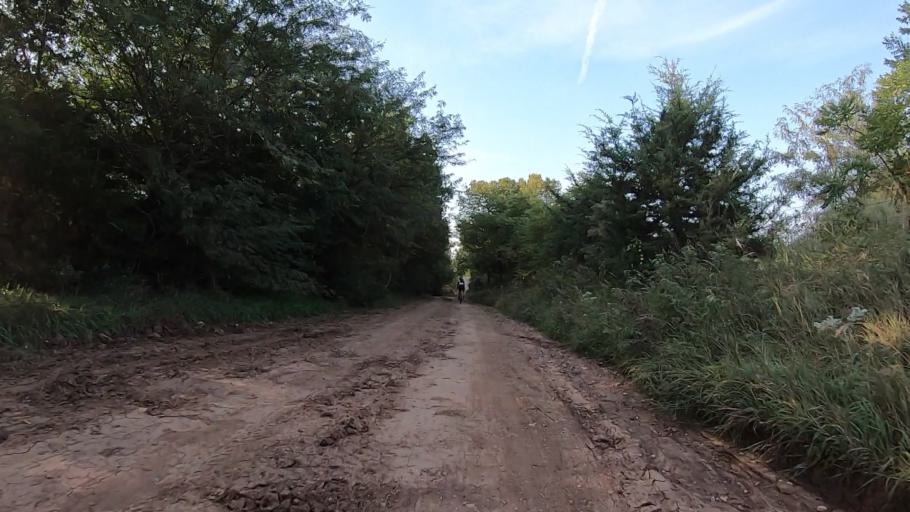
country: US
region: Kansas
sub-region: Marshall County
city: Blue Rapids
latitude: 39.7581
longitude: -96.7507
